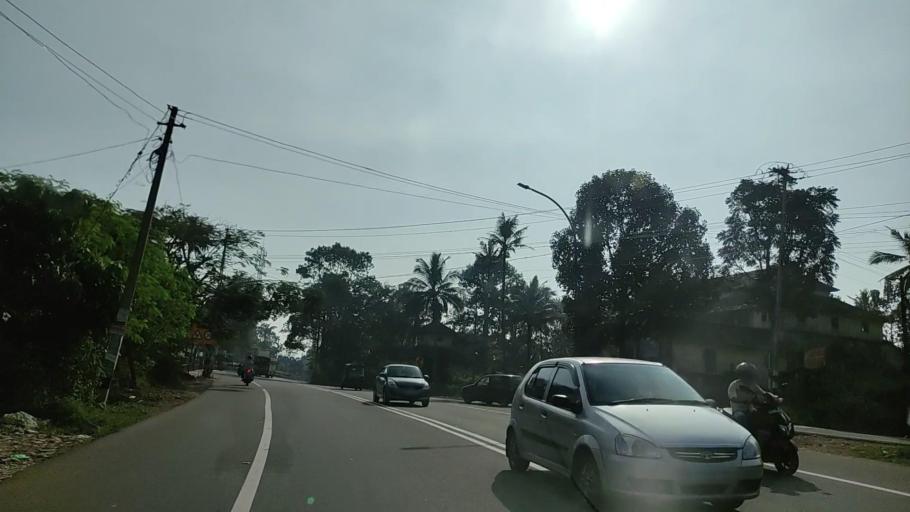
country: IN
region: Kerala
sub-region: Kollam
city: Punalur
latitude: 8.9792
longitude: 76.8118
